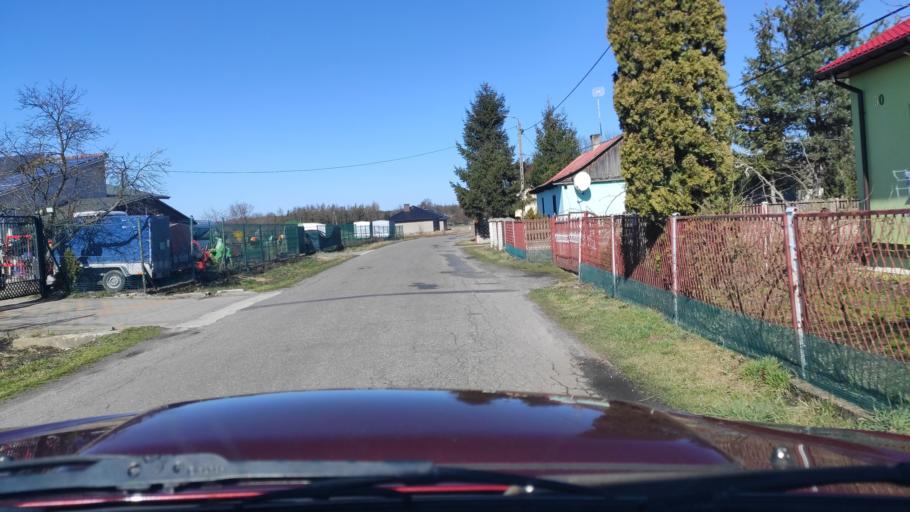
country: PL
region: Masovian Voivodeship
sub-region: Powiat zwolenski
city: Zwolen
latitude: 51.3808
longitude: 21.5796
